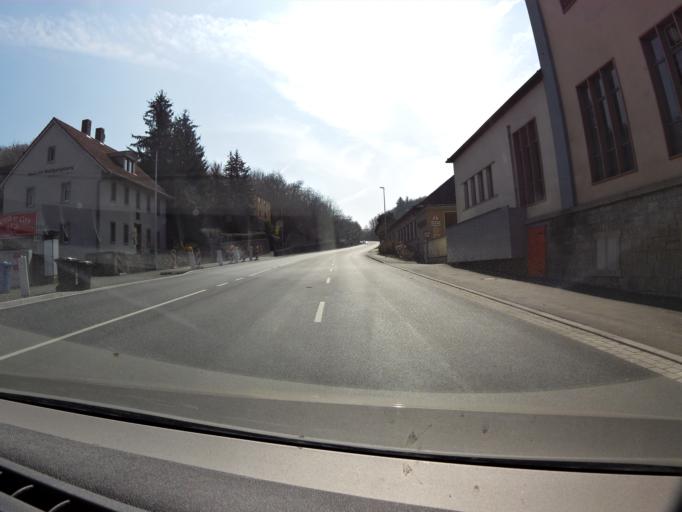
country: DE
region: Bavaria
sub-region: Regierungsbezirk Unterfranken
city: Ochsenfurt
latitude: 49.6601
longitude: 10.0712
